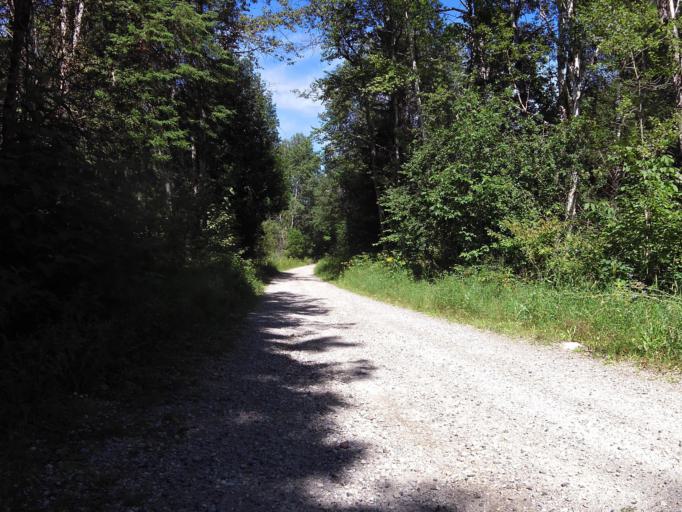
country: CA
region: Ontario
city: Renfrew
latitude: 45.0721
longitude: -76.7225
